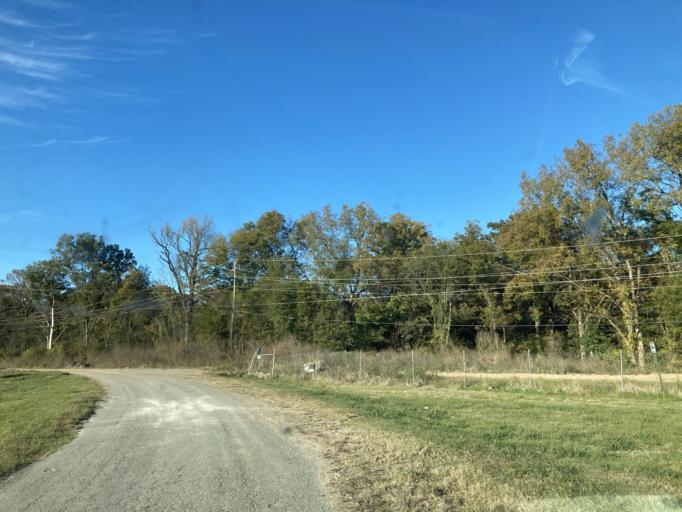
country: US
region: Mississippi
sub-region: Yazoo County
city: Yazoo City
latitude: 32.8826
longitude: -90.4203
